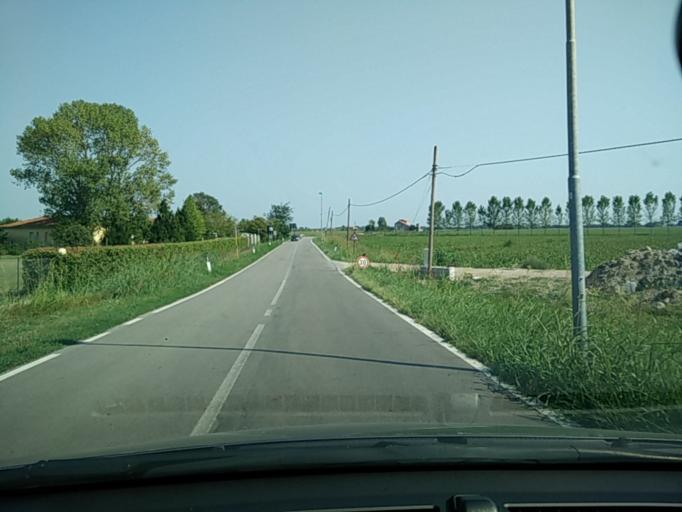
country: IT
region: Veneto
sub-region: Provincia di Venezia
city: La Salute di Livenza
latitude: 45.6445
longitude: 12.8231
